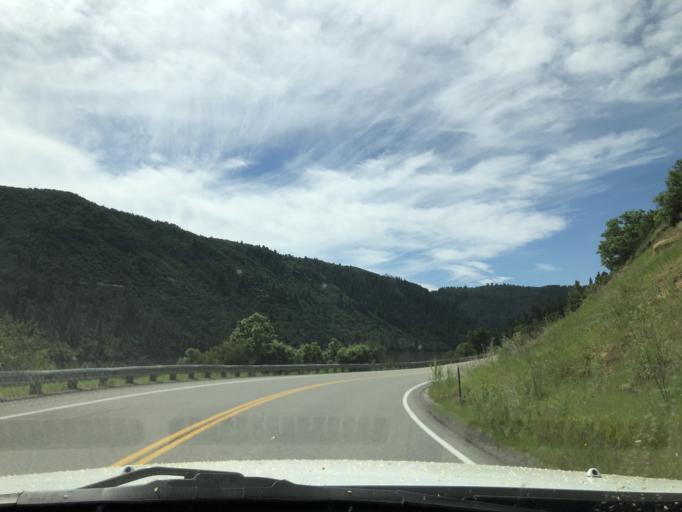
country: US
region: Colorado
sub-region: Delta County
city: Paonia
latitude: 38.9724
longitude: -107.3411
